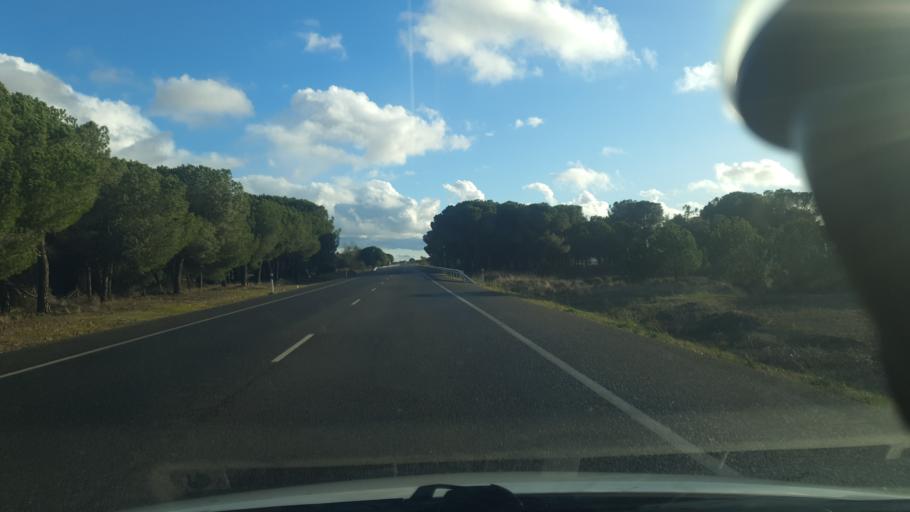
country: ES
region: Castille and Leon
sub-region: Provincia de Segovia
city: Codorniz
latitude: 41.0677
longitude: -4.6326
